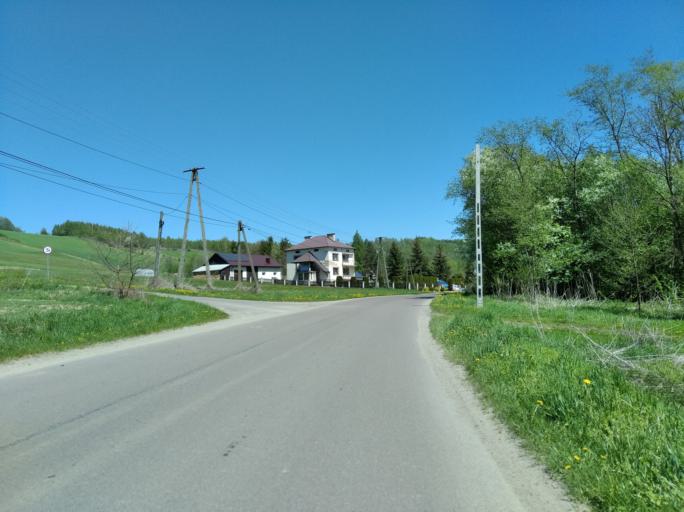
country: PL
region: Subcarpathian Voivodeship
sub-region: Powiat debicki
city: Brzostek
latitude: 49.9238
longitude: 21.3878
